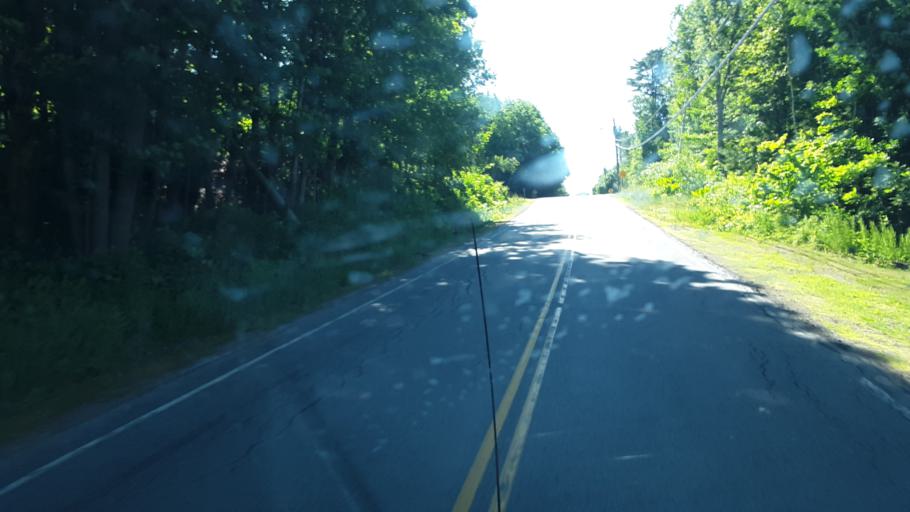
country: US
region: New Hampshire
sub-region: Grafton County
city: North Haverhill
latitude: 44.0812
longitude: -71.9995
